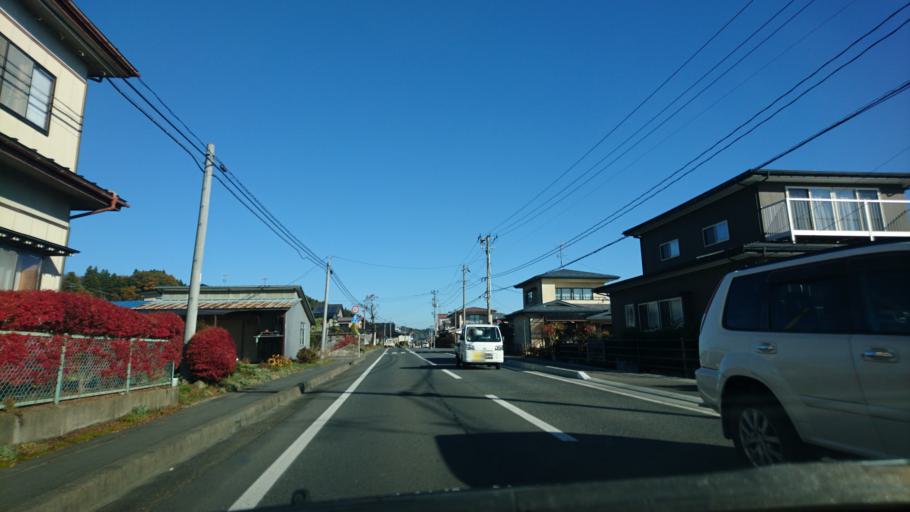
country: JP
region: Iwate
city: Mizusawa
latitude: 39.0598
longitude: 141.1245
